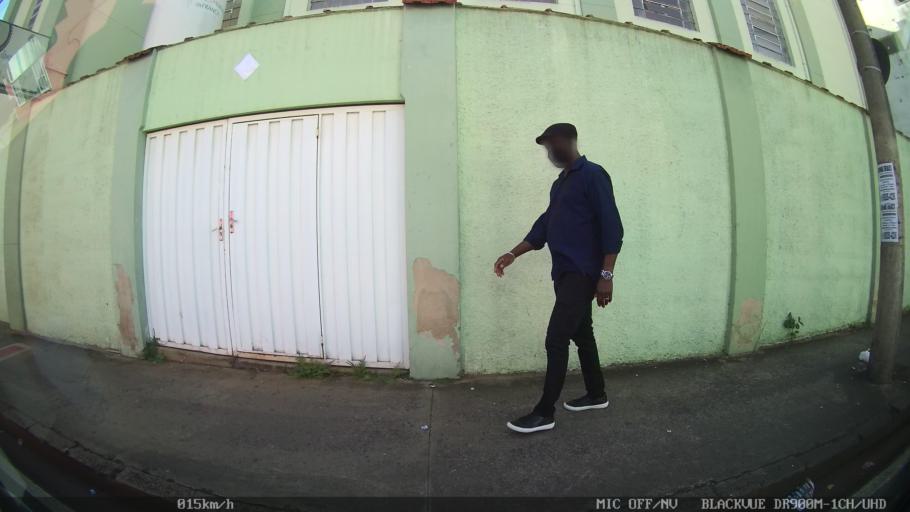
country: BR
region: Sao Paulo
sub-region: Franca
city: Franca
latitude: -20.5350
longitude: -47.4003
